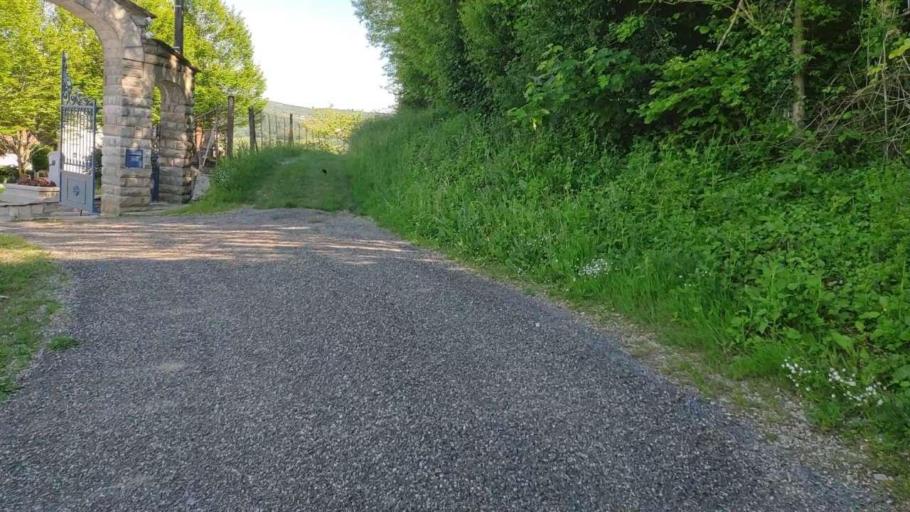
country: FR
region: Franche-Comte
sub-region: Departement du Jura
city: Perrigny
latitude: 46.7152
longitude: 5.5774
